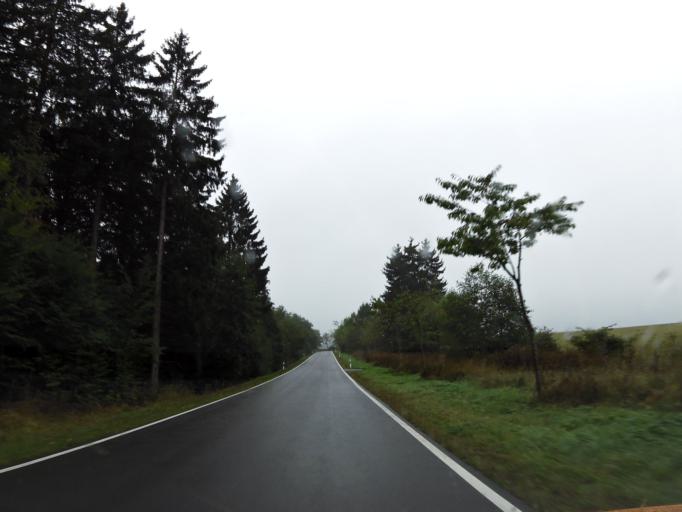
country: DE
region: Saxony-Anhalt
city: Hasselfelde
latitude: 51.6554
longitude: 10.8652
